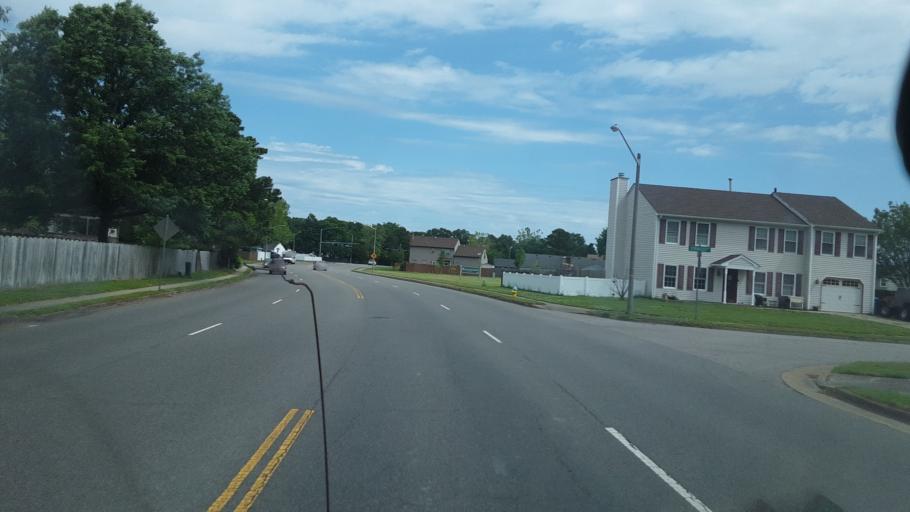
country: US
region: Virginia
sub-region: City of Virginia Beach
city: Virginia Beach
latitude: 36.7707
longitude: -75.9985
